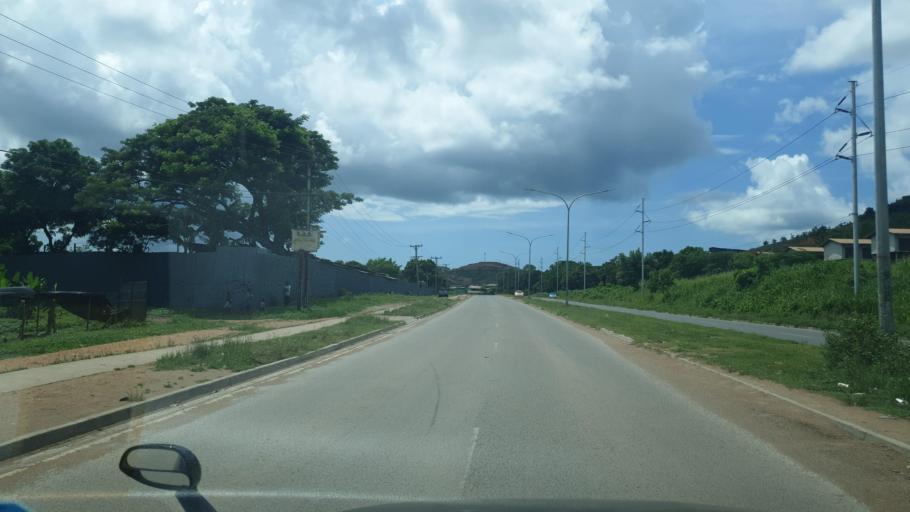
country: PG
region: National Capital
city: Port Moresby
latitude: -9.3901
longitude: 147.1533
